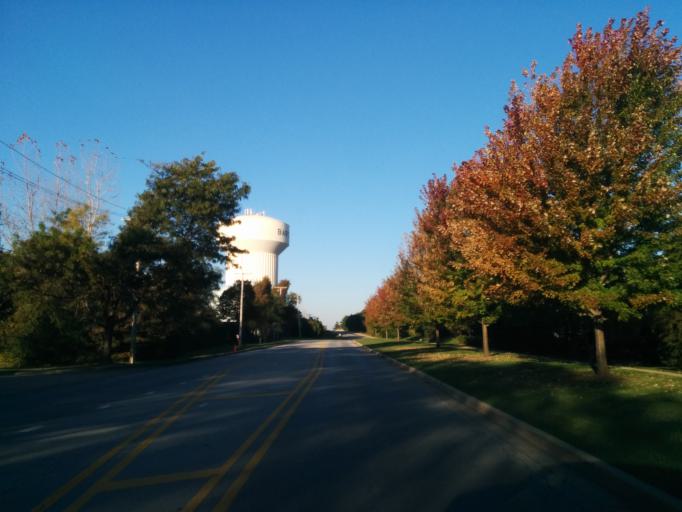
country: US
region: Illinois
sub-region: DuPage County
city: Carol Stream
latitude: 41.9518
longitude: -88.1623
